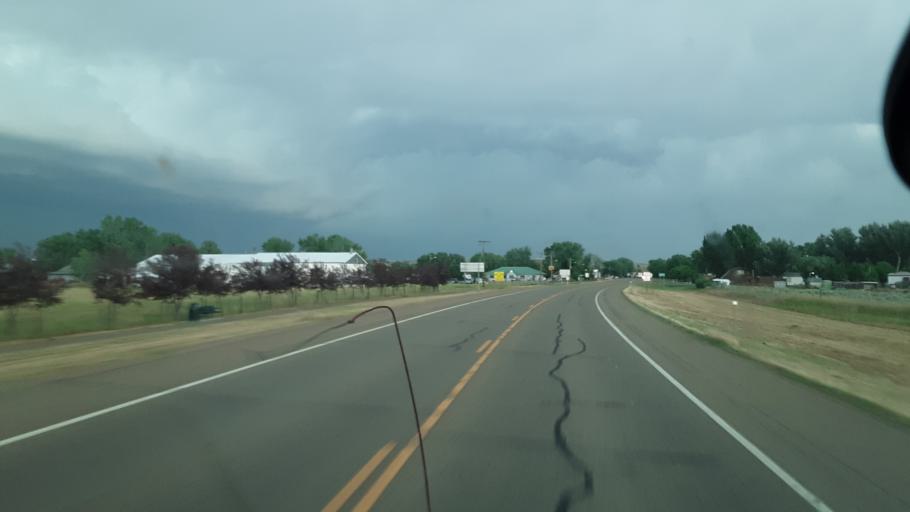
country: US
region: Montana
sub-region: Powder River County
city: Broadus
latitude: 45.4329
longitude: -105.4081
